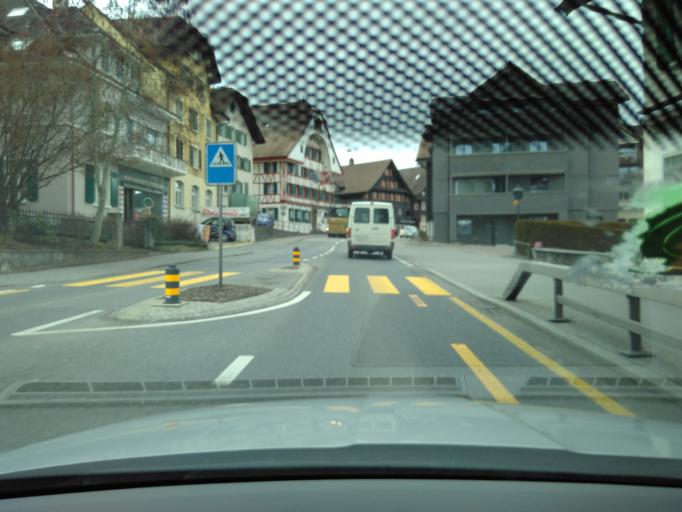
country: CH
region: Lucerne
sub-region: Hochdorf District
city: Emmen
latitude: 47.0930
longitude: 8.2723
